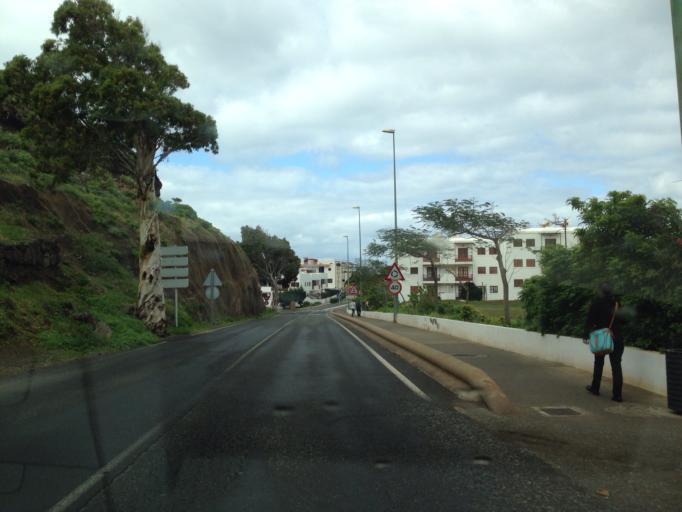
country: ES
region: Canary Islands
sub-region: Provincia de Las Palmas
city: Agaete
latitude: 28.1014
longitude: -15.7084
